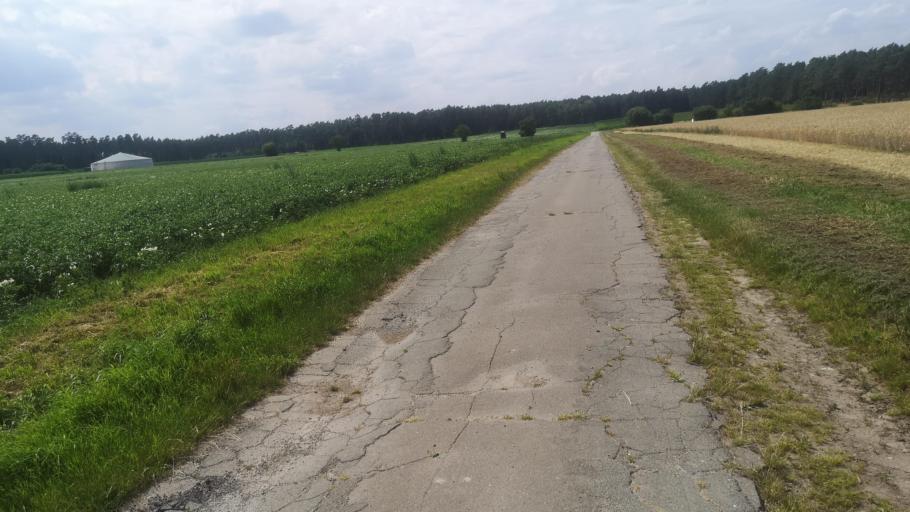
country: DE
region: Lower Saxony
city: Dahlem
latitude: 53.2334
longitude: 10.7365
